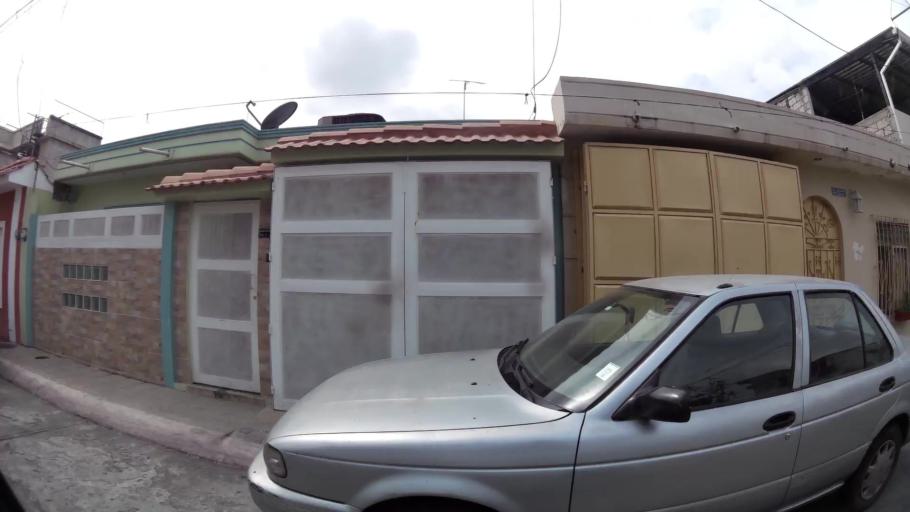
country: EC
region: Guayas
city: Eloy Alfaro
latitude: -2.1190
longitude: -79.8983
